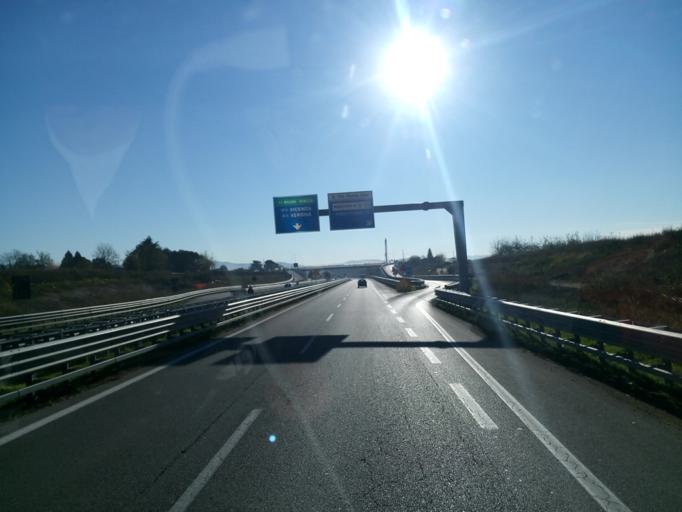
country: IT
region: Veneto
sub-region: Provincia di Vicenza
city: Montecchio Maggiore-Alte Ceccato
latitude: 45.5049
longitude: 11.3930
